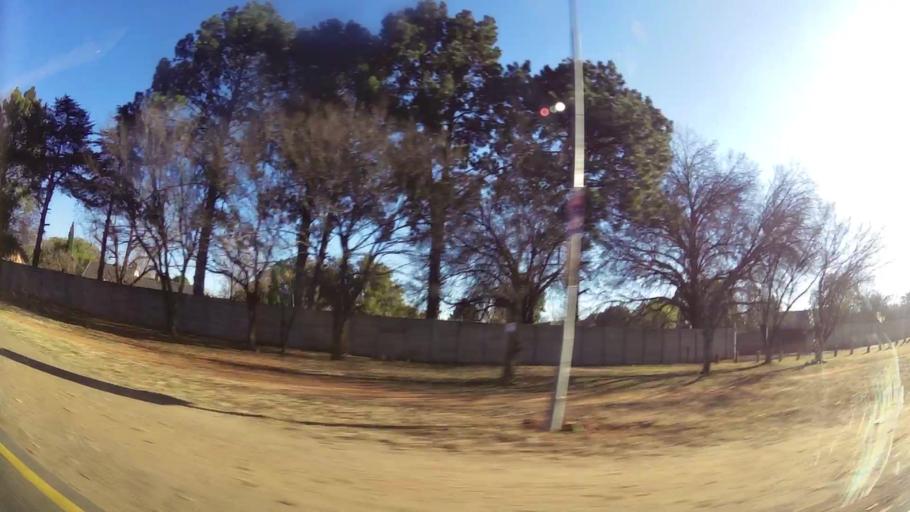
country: ZA
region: Gauteng
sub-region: Ekurhuleni Metropolitan Municipality
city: Tembisa
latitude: -26.0394
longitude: 28.2501
